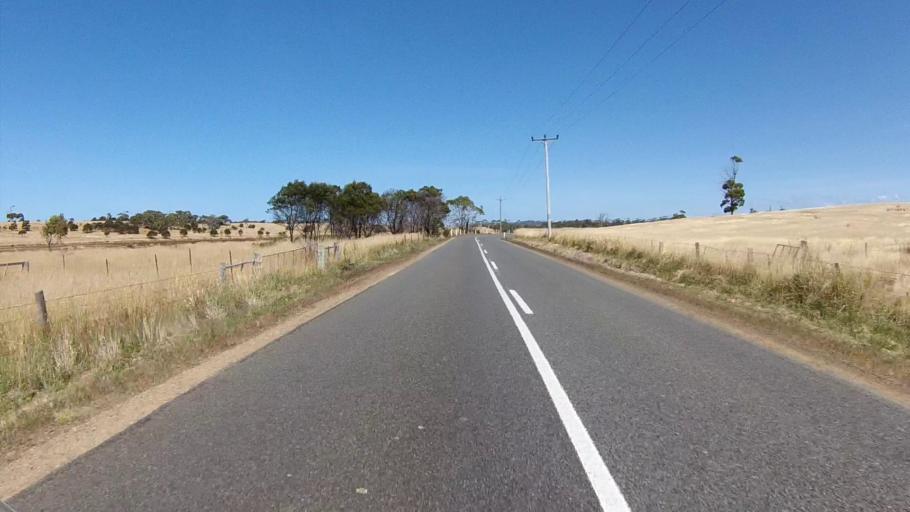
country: AU
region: Tasmania
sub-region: Sorell
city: Sorell
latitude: -42.2750
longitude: 148.0042
